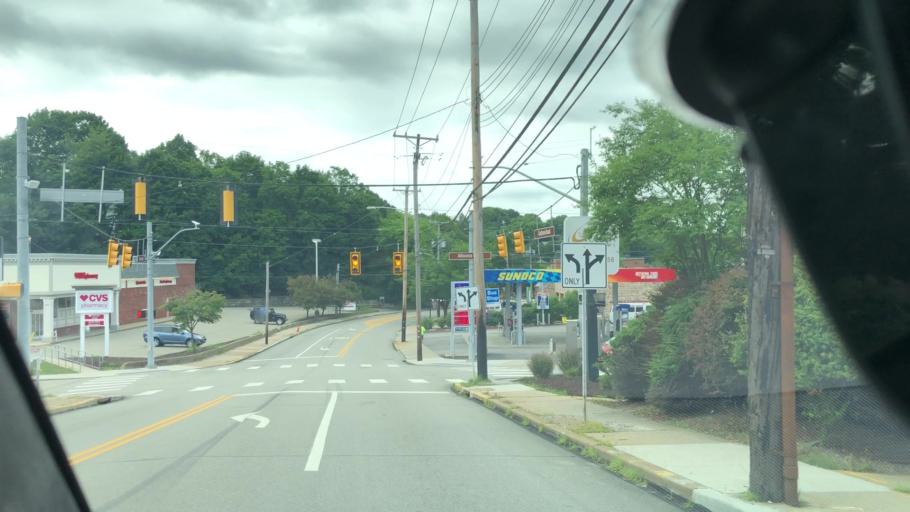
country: US
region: Pennsylvania
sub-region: Allegheny County
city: Dormont
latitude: 40.3832
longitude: -80.0526
